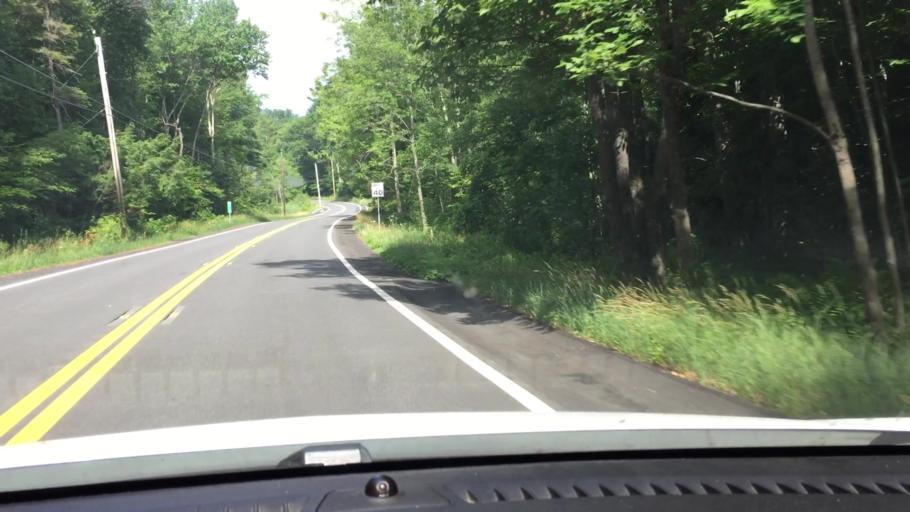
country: US
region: Massachusetts
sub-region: Berkshire County
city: Otis
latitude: 42.1929
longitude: -73.1234
